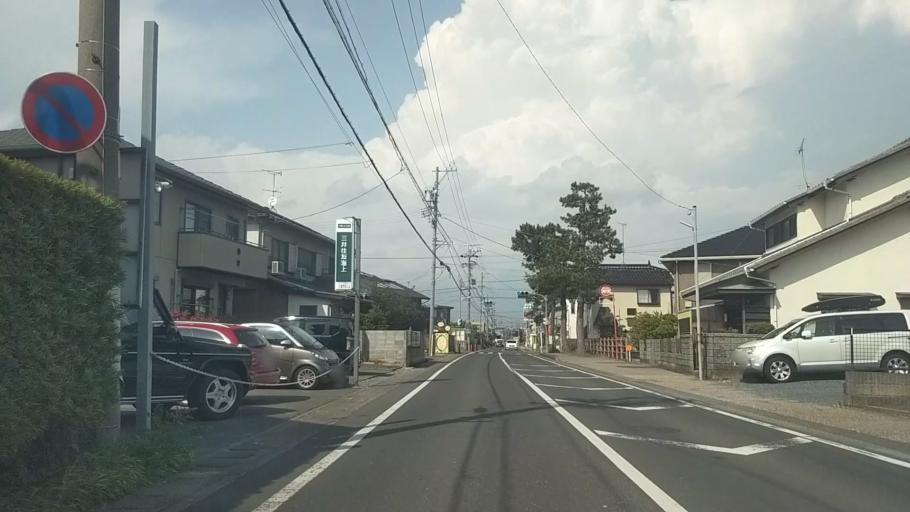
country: JP
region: Shizuoka
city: Hamamatsu
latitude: 34.7212
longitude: 137.7804
